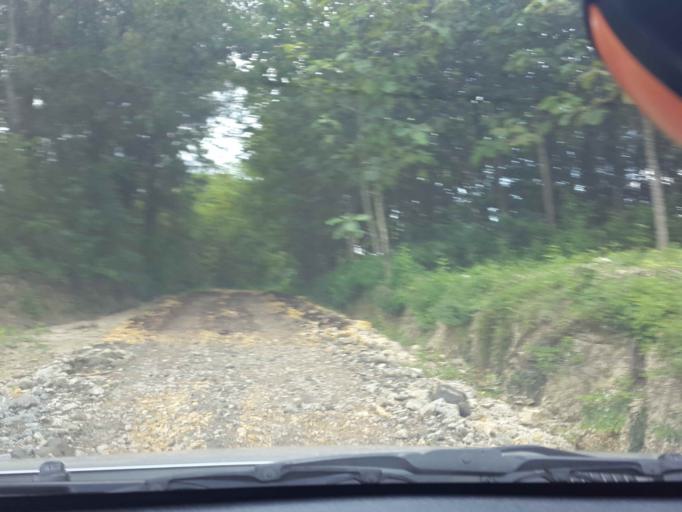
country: ID
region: Central Java
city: Sragen
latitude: -7.2999
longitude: 110.9773
